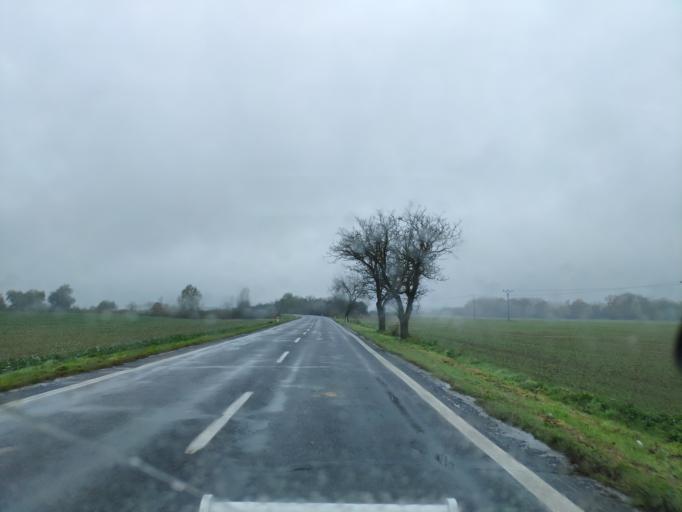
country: SK
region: Kosicky
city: Cierna nad Tisou
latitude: 48.4477
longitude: 21.9917
